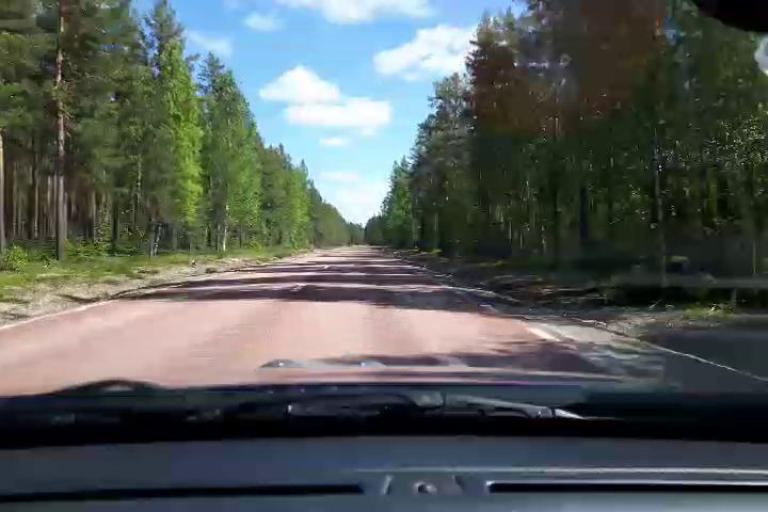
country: SE
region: Gaevleborg
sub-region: Ljusdals Kommun
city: Farila
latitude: 61.9245
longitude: 15.5880
